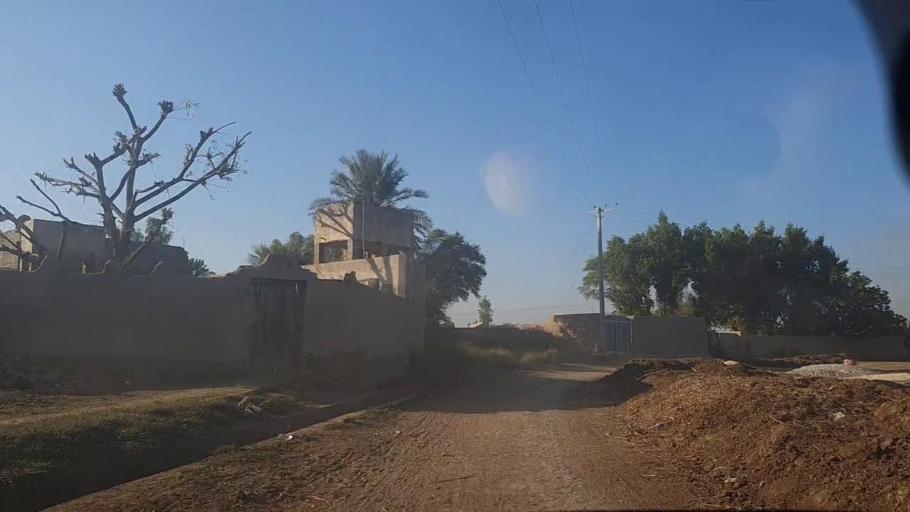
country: PK
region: Sindh
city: Sobhadero
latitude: 27.4005
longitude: 68.4211
